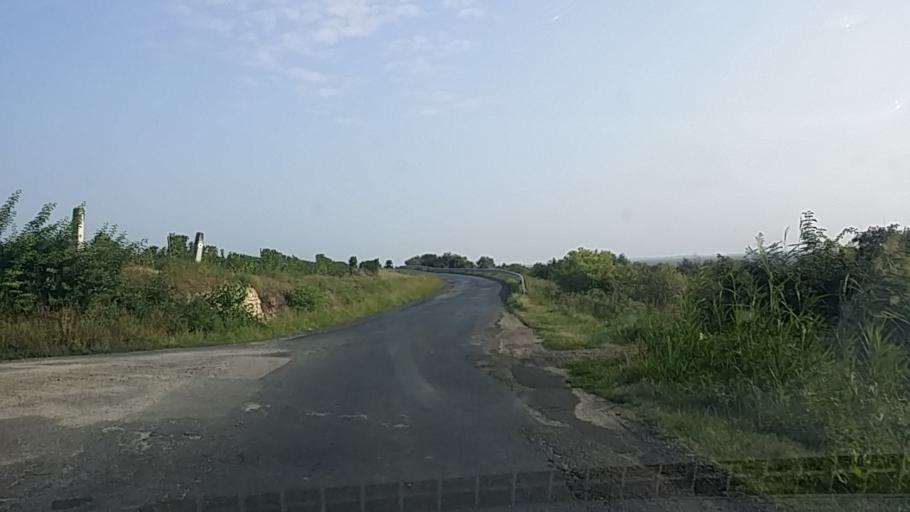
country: HU
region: Gyor-Moson-Sopron
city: Fertorakos
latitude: 47.6730
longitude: 16.6727
